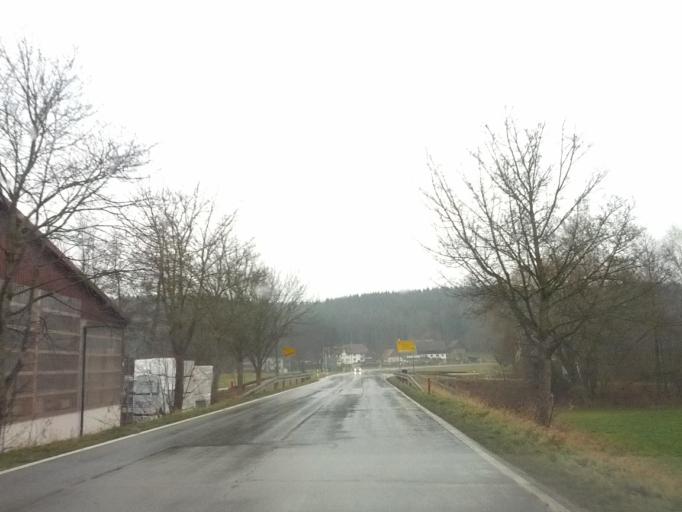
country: DE
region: Baden-Wuerttemberg
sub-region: Tuebingen Region
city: Rot an der Rot
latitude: 48.0142
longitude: 10.0259
